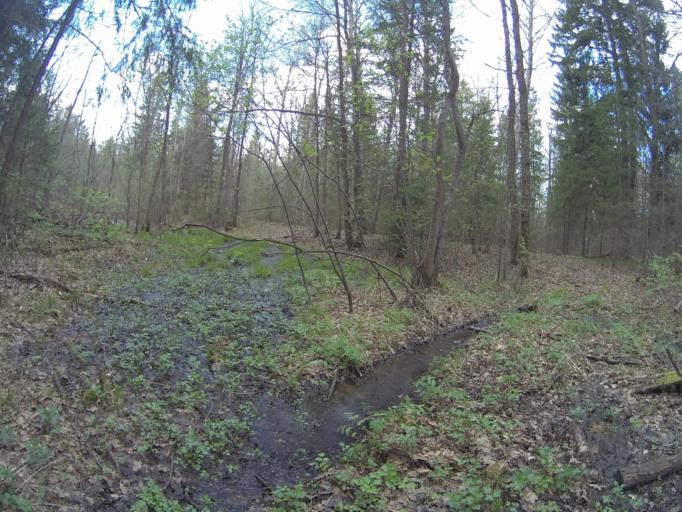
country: RU
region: Vladimir
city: Raduzhnyy
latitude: 56.0372
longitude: 40.3791
